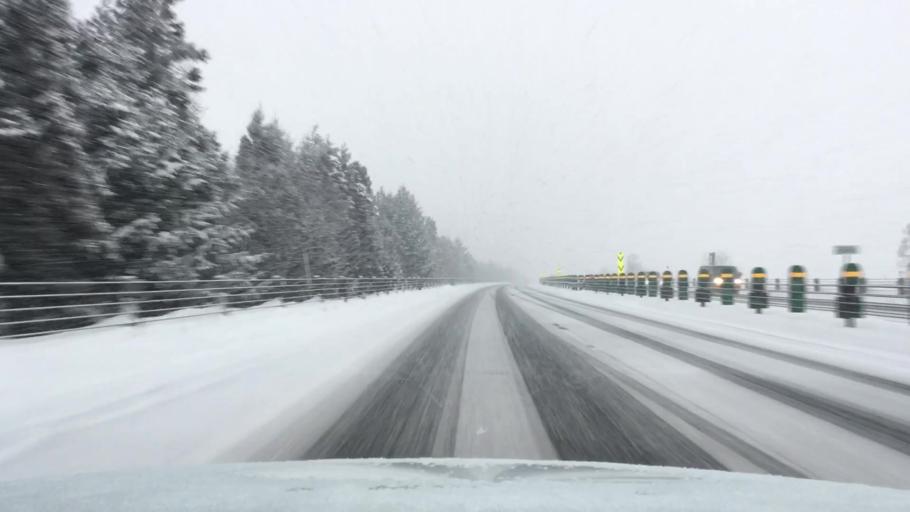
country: JP
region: Akita
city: Hanawa
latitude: 40.2231
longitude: 140.7889
